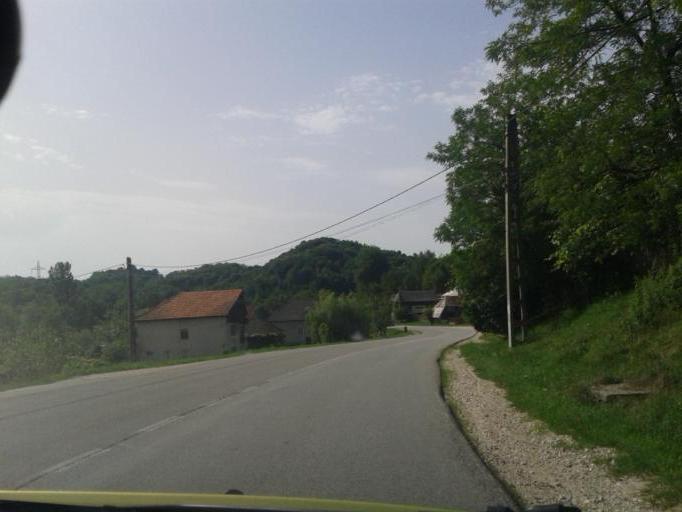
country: RO
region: Valcea
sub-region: Comuna Pietrari
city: Pietrarii de Sus
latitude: 45.1339
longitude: 24.0854
